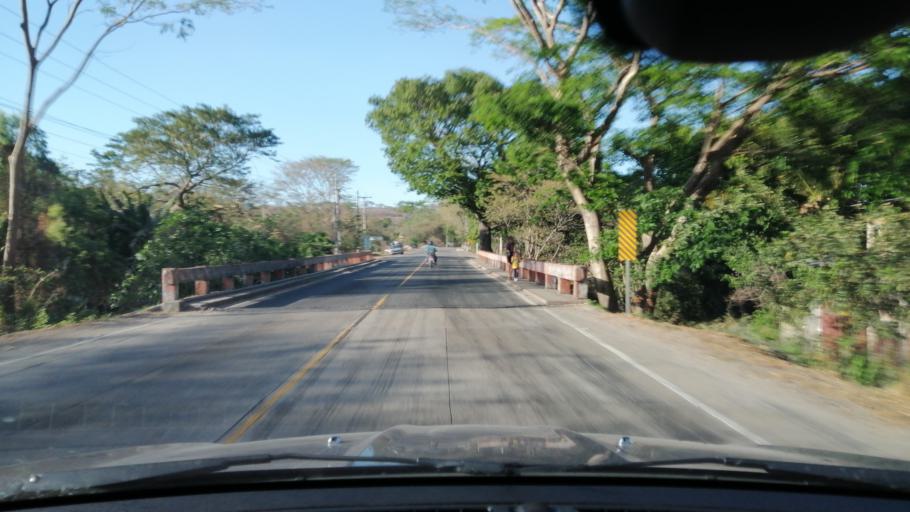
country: SV
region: Santa Ana
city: Texistepeque
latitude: 14.2147
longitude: -89.4970
